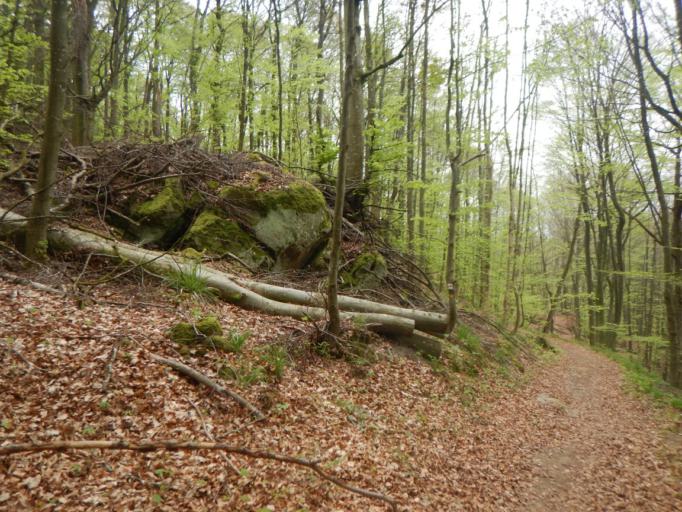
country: LU
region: Grevenmacher
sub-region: Canton d'Echternach
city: Waldbillig
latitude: 49.7975
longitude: 6.3168
